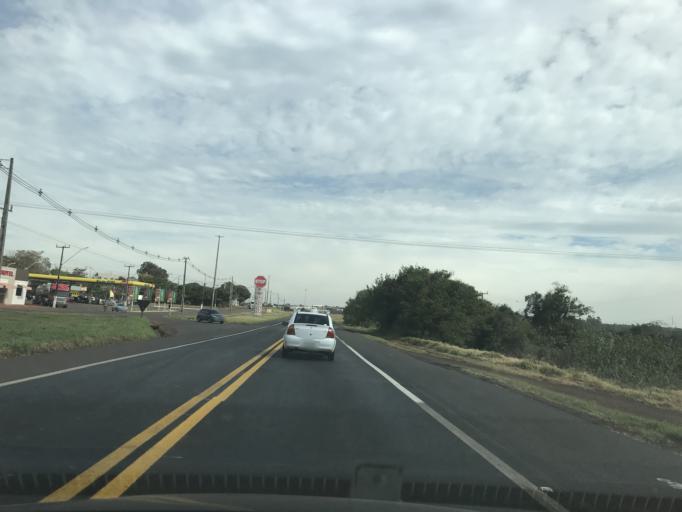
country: BR
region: Parana
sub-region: Cascavel
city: Cascavel
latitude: -25.0449
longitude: -53.6081
